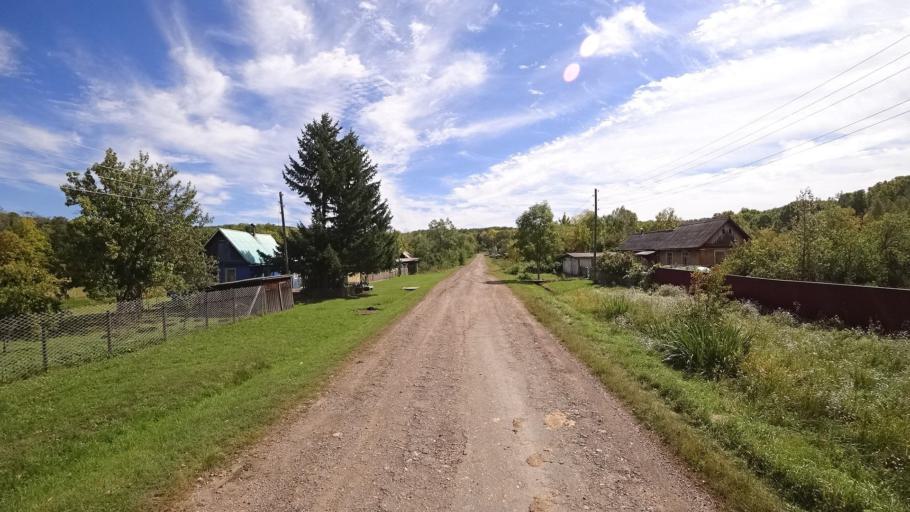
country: RU
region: Primorskiy
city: Yakovlevka
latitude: 44.6544
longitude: 133.7456
